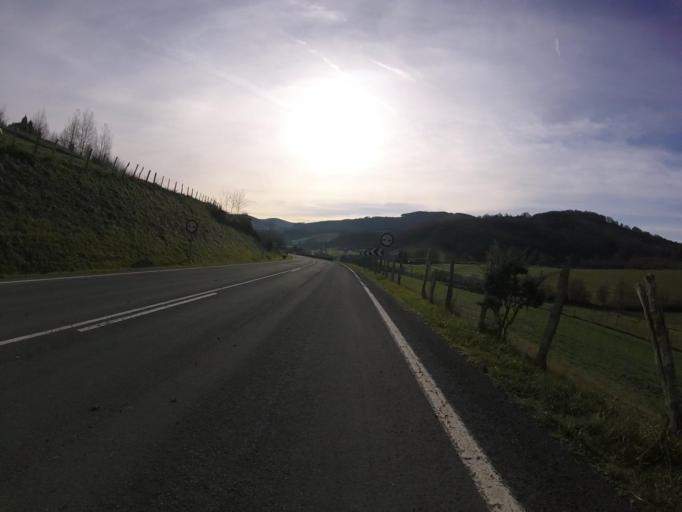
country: ES
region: Basque Country
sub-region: Provincia de Guipuzcoa
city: Berastegui
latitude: 43.1167
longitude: -1.9671
